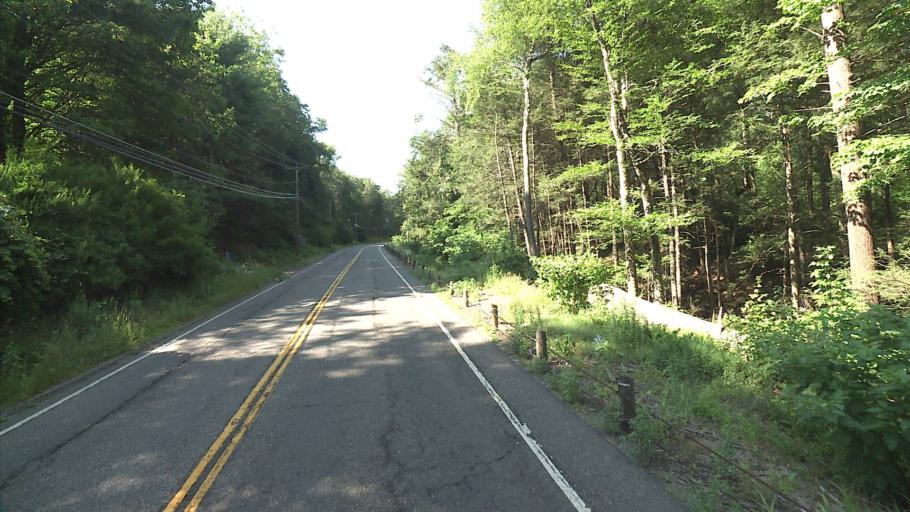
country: US
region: Connecticut
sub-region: Litchfield County
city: Winsted
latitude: 41.9560
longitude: -73.0280
